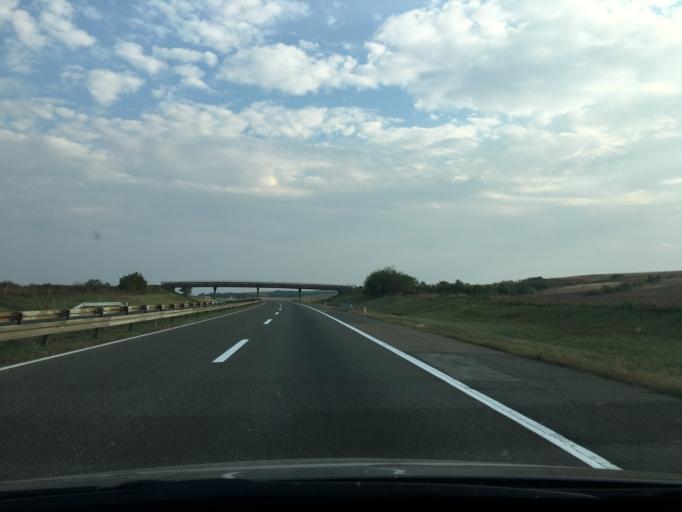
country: RS
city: Lugavcina
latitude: 44.5167
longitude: 21.0122
